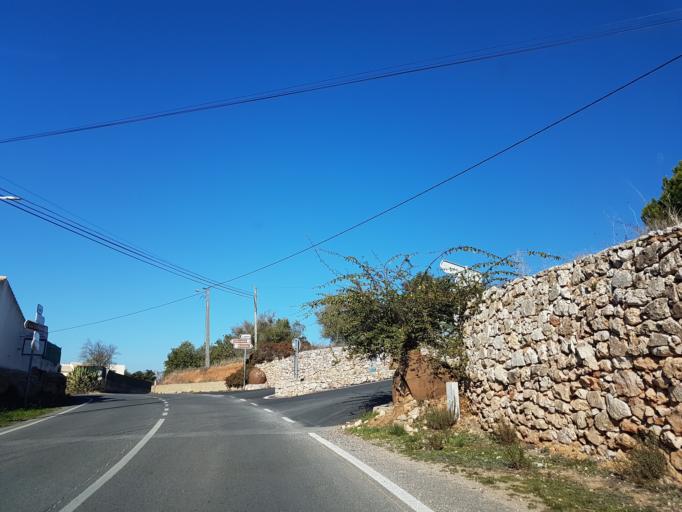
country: PT
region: Faro
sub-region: Lagoa
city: Carvoeiro
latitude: 37.1106
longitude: -8.4459
